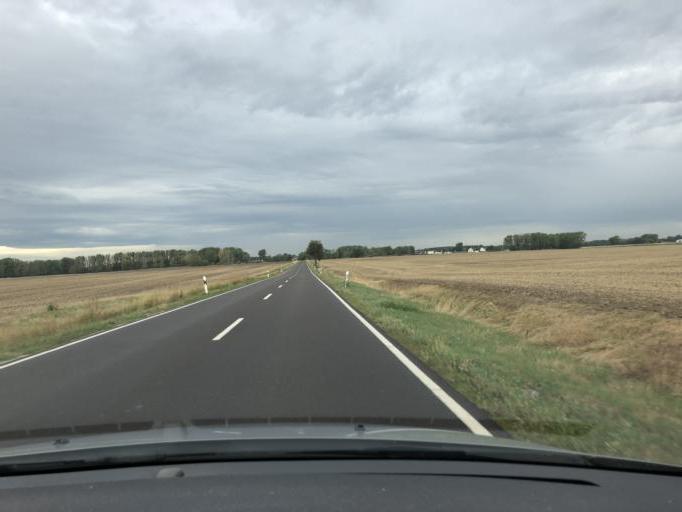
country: DE
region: Saxony-Anhalt
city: Calbe
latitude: 51.8867
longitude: 11.8157
